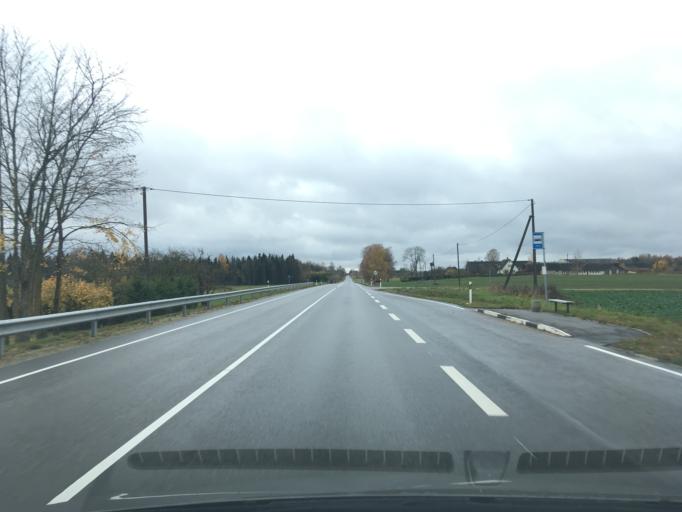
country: EE
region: Jogevamaa
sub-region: Tabivere vald
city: Tabivere
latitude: 58.4569
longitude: 26.5326
